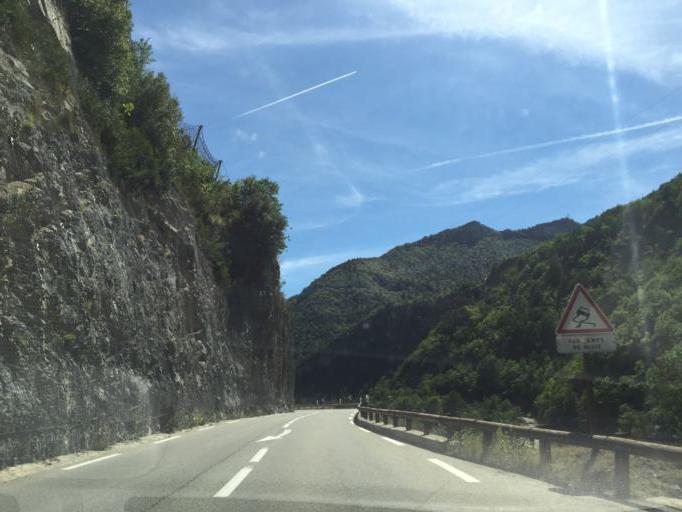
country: FR
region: Provence-Alpes-Cote d'Azur
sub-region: Departement des Alpes-Maritimes
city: Saint-Martin-Vesubie
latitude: 44.0443
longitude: 7.1285
